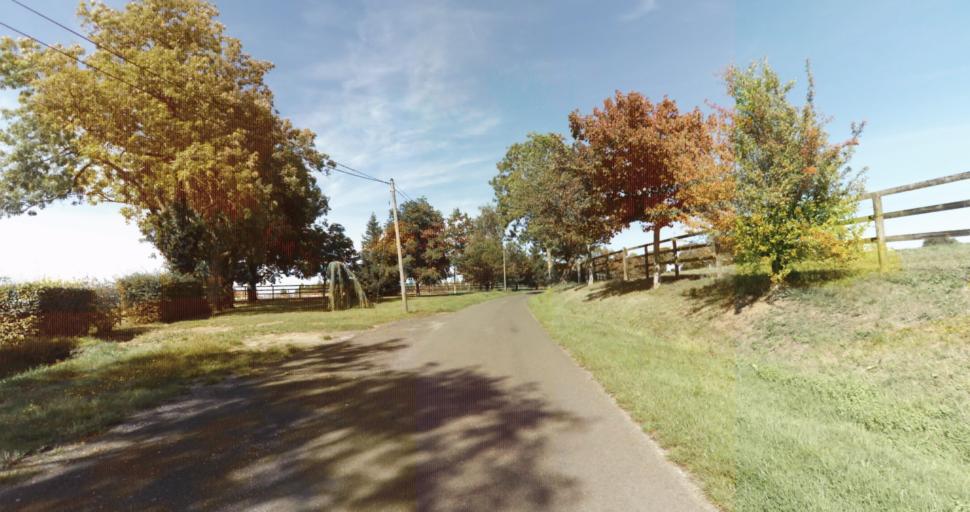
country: FR
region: Lower Normandy
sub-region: Departement de l'Orne
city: Gace
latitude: 48.7576
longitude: 0.2361
